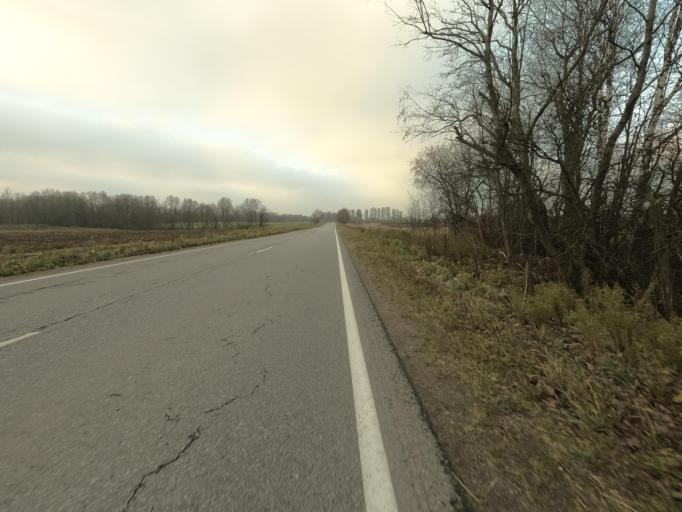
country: RU
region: Leningrad
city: Mga
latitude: 59.7671
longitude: 31.0203
